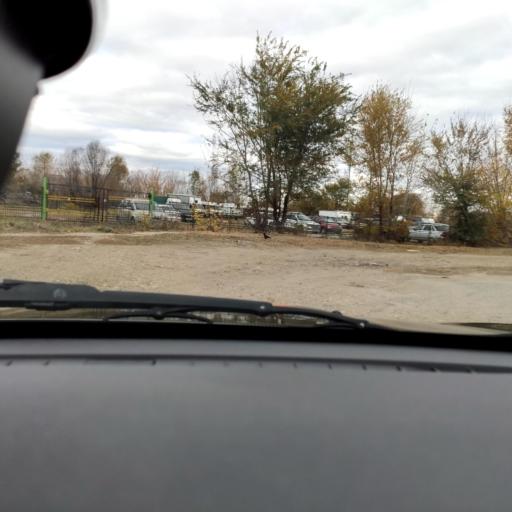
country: RU
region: Samara
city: Tol'yatti
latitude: 53.5476
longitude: 49.3217
